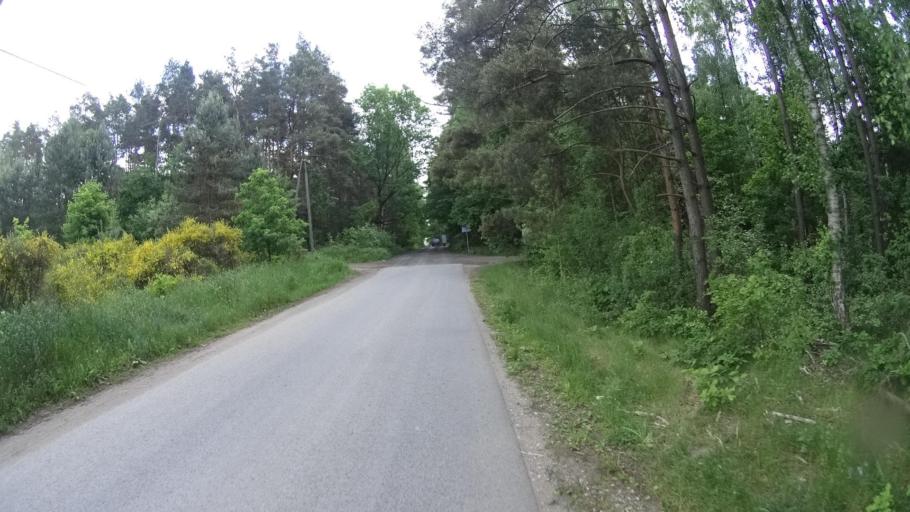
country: PL
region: Masovian Voivodeship
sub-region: Powiat pruszkowski
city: Nadarzyn
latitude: 52.0664
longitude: 20.8201
